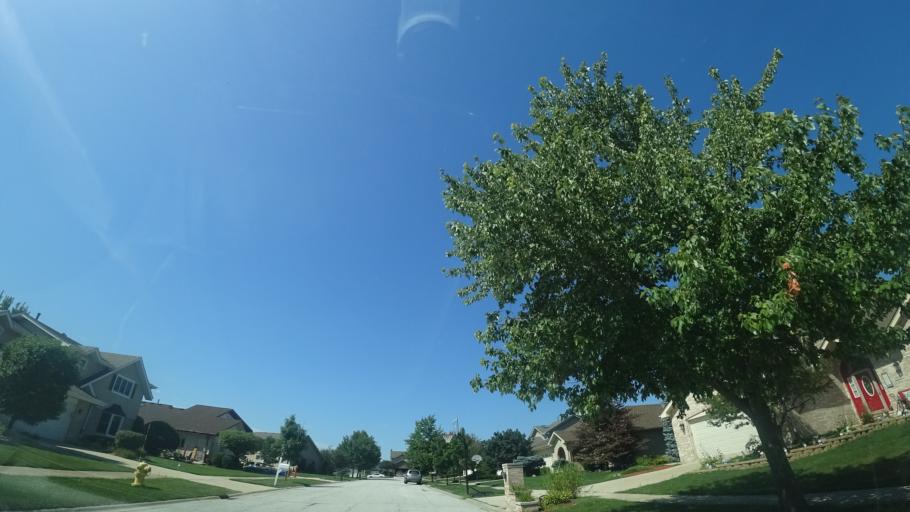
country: US
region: Illinois
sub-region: Will County
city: Homer Glen
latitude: 41.5685
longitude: -87.9071
